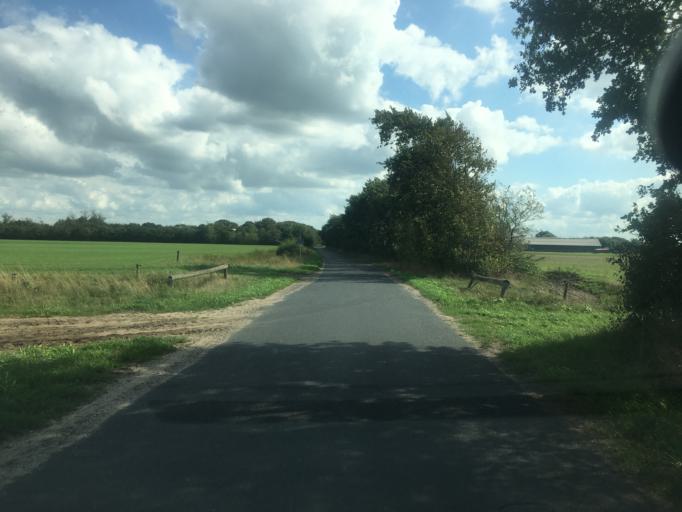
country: DK
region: South Denmark
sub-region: Tonder Kommune
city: Logumkloster
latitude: 55.0036
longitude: 9.0128
